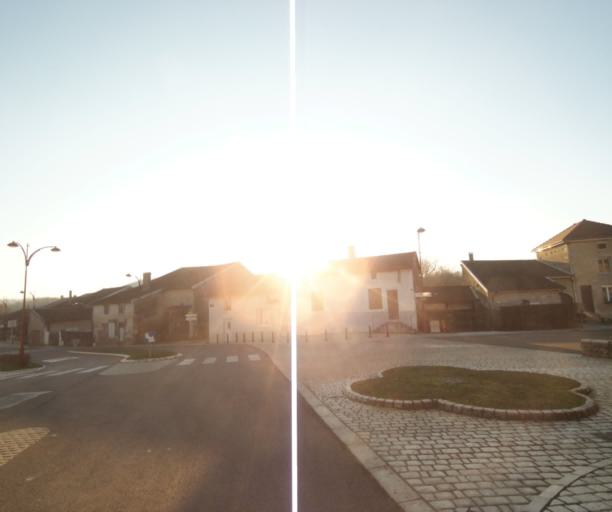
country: FR
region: Champagne-Ardenne
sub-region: Departement de la Haute-Marne
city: Chevillon
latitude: 48.5443
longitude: 5.1021
